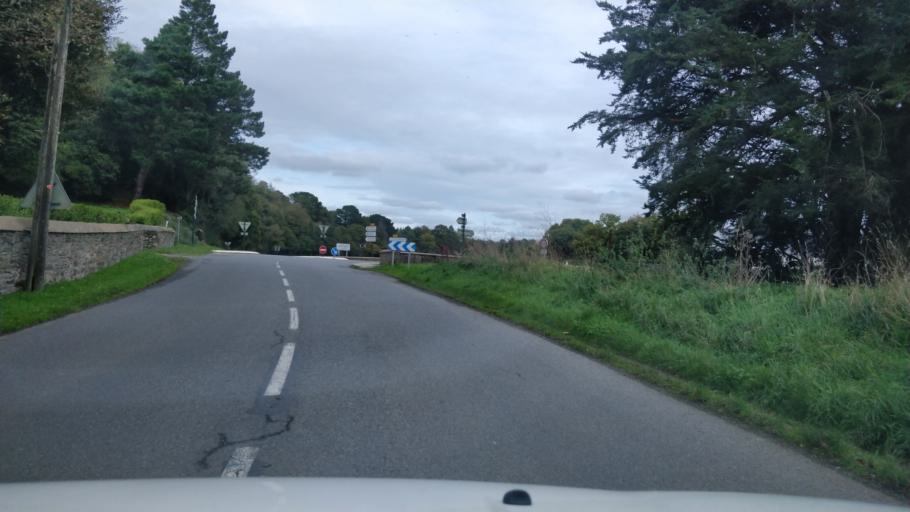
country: FR
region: Brittany
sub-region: Departement des Cotes-d'Armor
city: La Roche-Derrien
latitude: 48.7495
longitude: -3.2681
